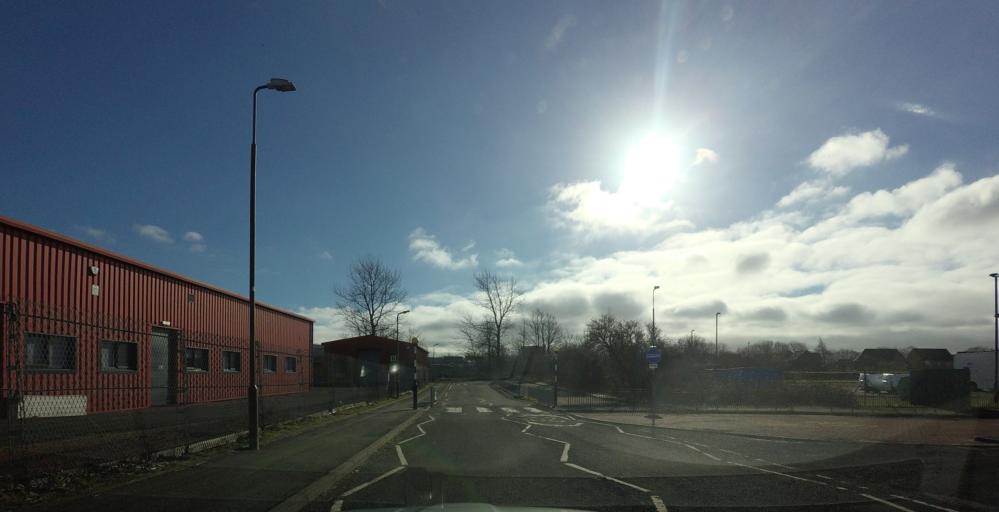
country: GB
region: Scotland
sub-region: West Lothian
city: Broxburn
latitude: 55.9320
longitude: -3.4843
